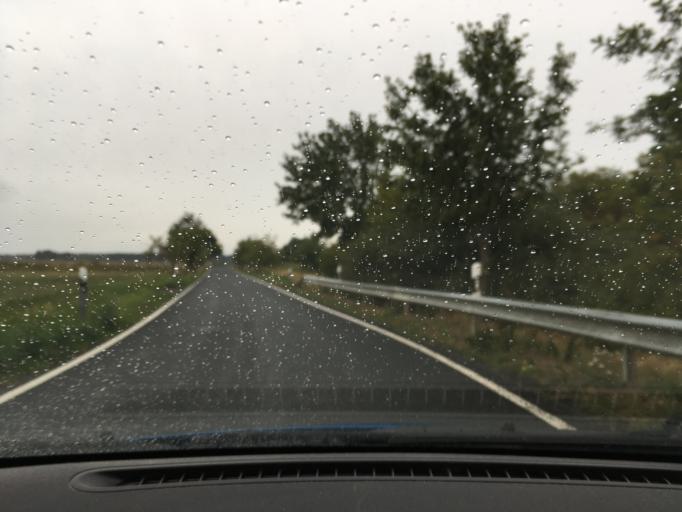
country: DE
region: Lower Saxony
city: Hitzacker
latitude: 53.1889
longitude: 11.0378
